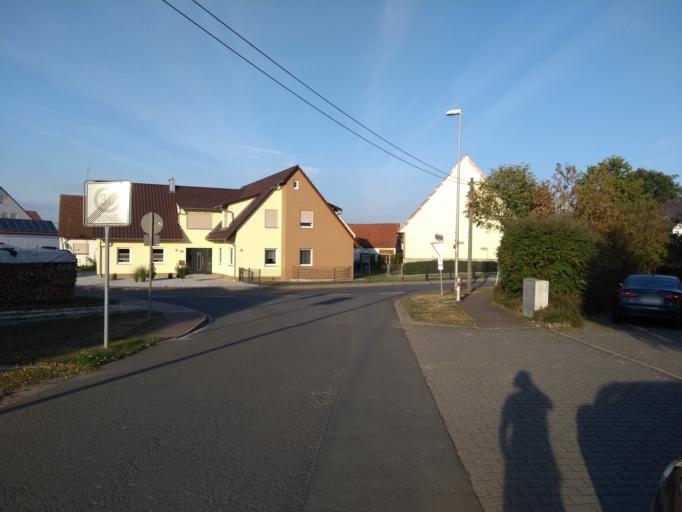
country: DE
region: Bavaria
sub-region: Regierungsbezirk Mittelfranken
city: Weisendorf
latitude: 49.5980
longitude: 10.8261
